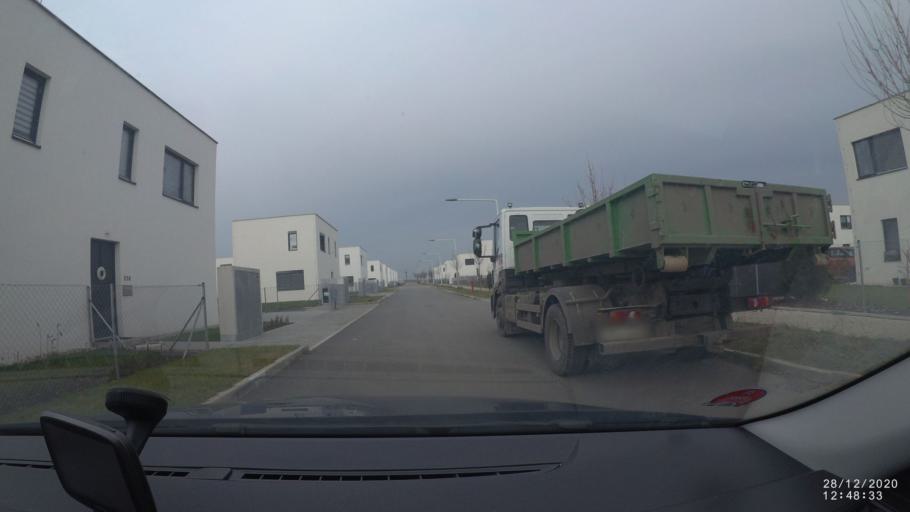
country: CZ
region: Praha
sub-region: Praha 19
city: Kbely
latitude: 50.1564
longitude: 14.5709
